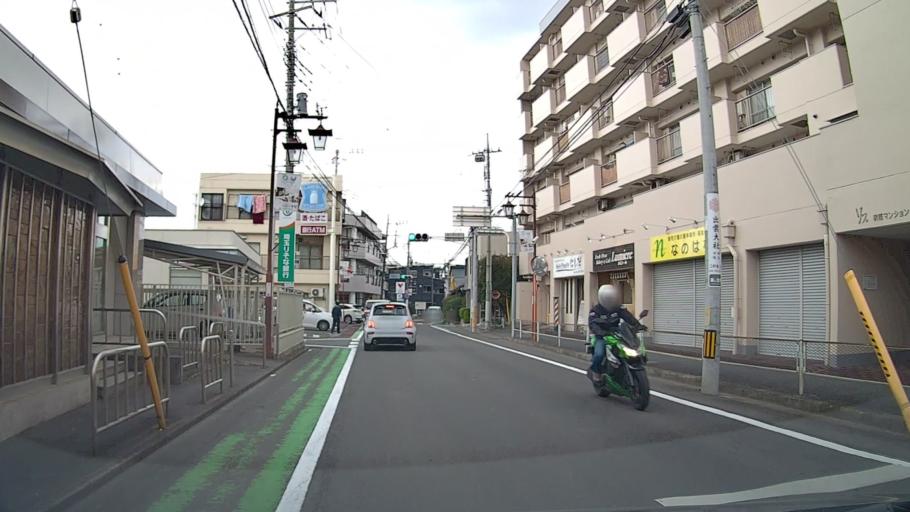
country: JP
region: Saitama
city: Asaka
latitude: 35.7975
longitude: 139.5949
